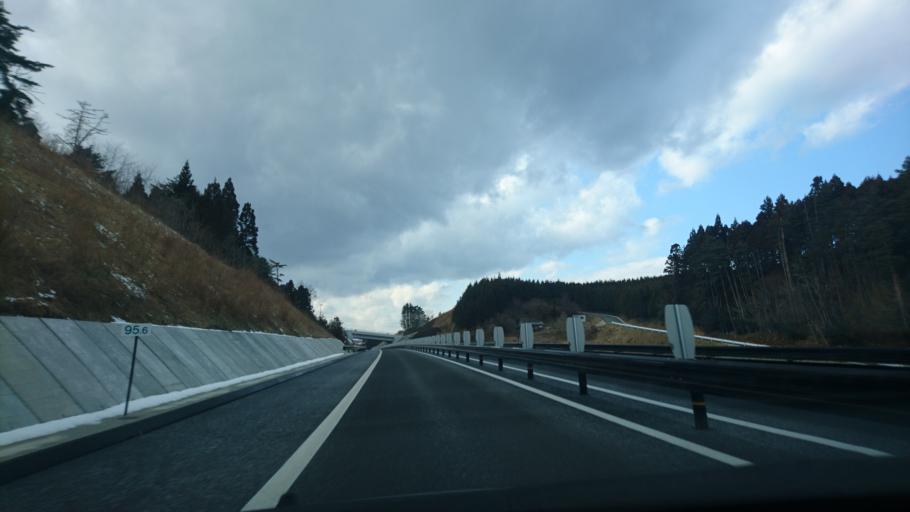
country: JP
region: Miyagi
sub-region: Oshika Gun
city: Onagawa Cho
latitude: 38.7560
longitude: 141.5099
